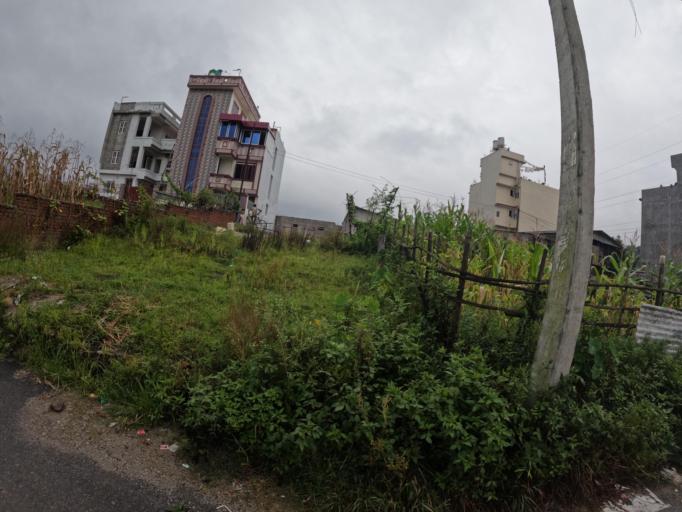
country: NP
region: Central Region
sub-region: Bagmati Zone
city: Kathmandu
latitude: 27.7639
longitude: 85.3194
